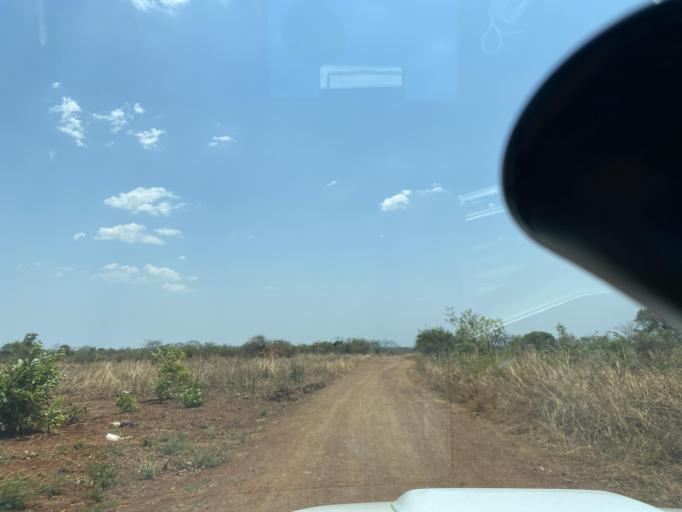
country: ZM
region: Lusaka
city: Lusaka
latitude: -15.5065
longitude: 28.0186
